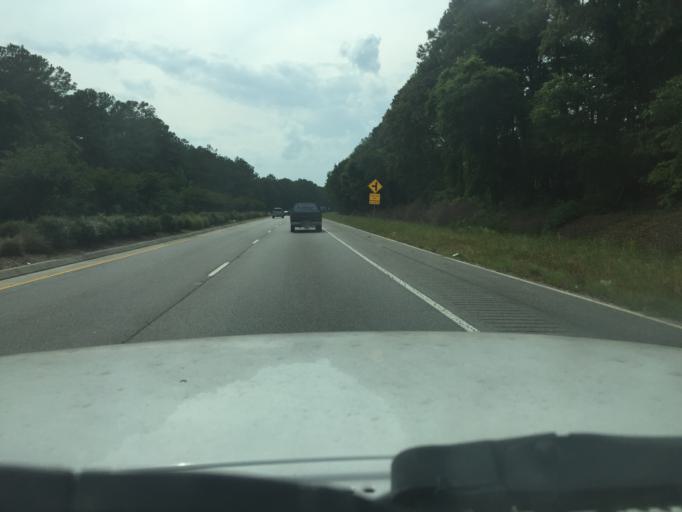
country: US
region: Georgia
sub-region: Chatham County
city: Wilmington Island
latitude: 32.0317
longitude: -80.9749
